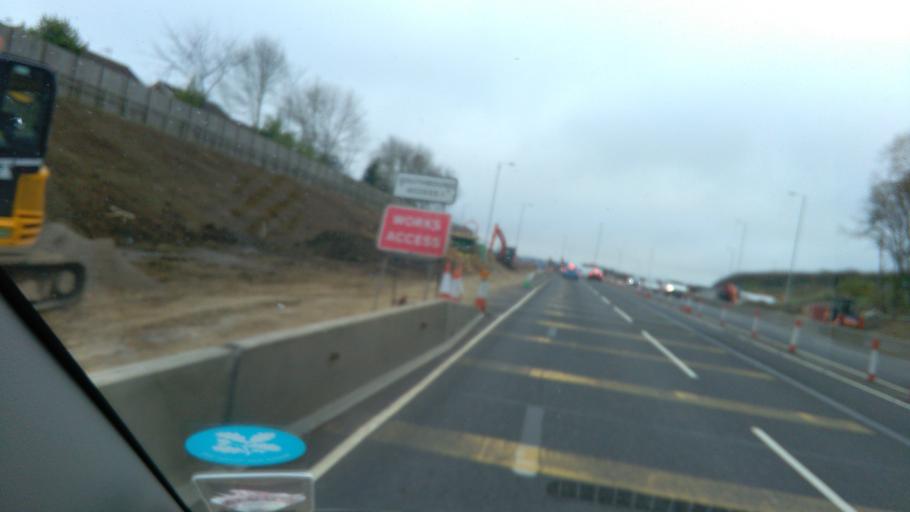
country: GB
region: England
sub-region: Northamptonshire
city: Towcester
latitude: 52.1311
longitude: -1.0036
